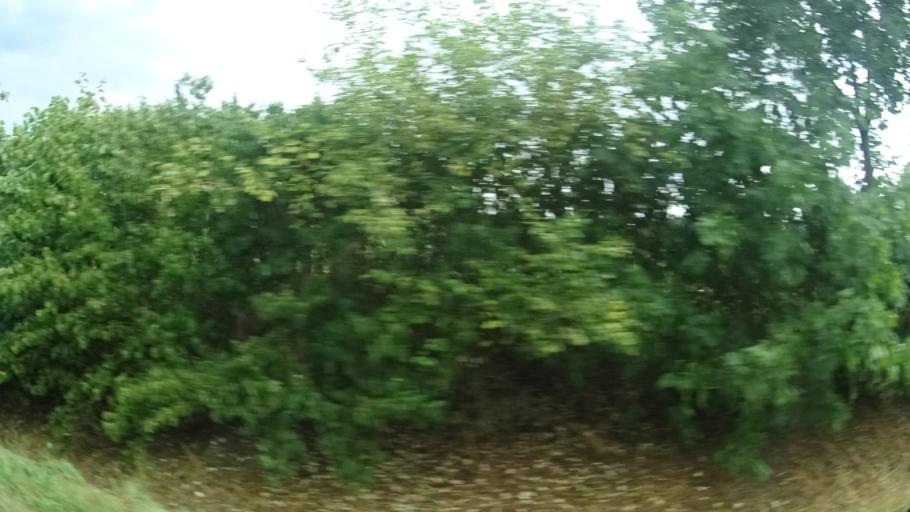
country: DE
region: Hesse
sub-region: Regierungsbezirk Kassel
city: Bad Hersfeld
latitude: 50.8229
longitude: 9.6745
